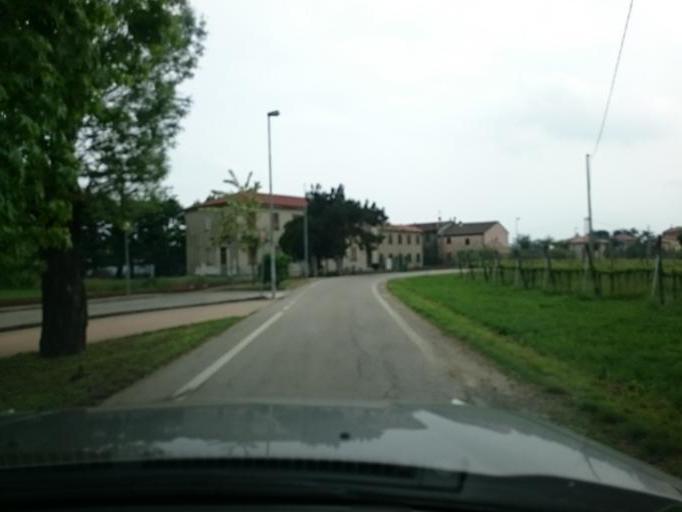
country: IT
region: Veneto
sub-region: Provincia di Padova
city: Battaglia Terme
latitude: 45.2748
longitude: 11.7595
